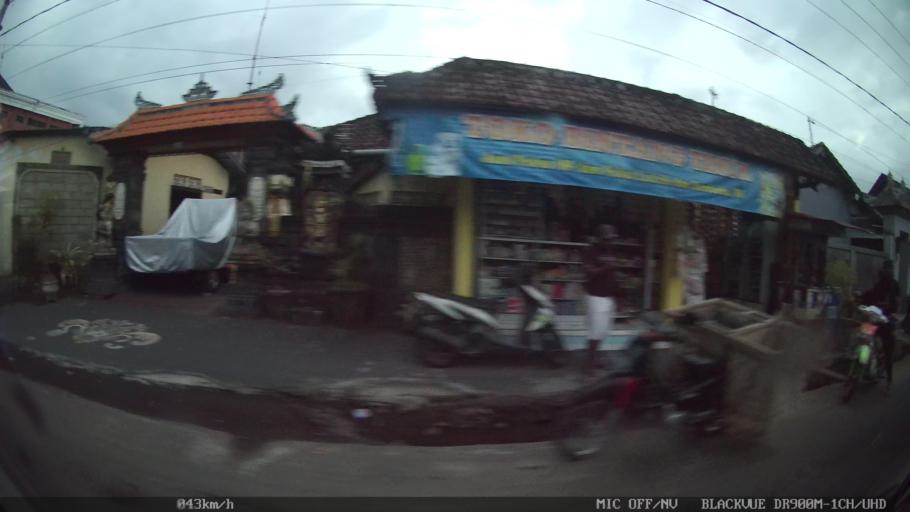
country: ID
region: Bali
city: Banjar Kertajiwa
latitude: -8.6391
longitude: 115.2727
